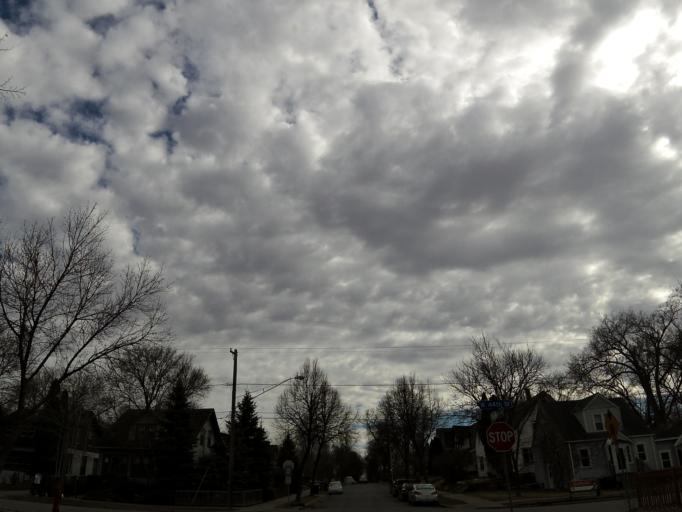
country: US
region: Minnesota
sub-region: Hennepin County
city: Saint Louis Park
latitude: 44.9236
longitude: -93.3227
